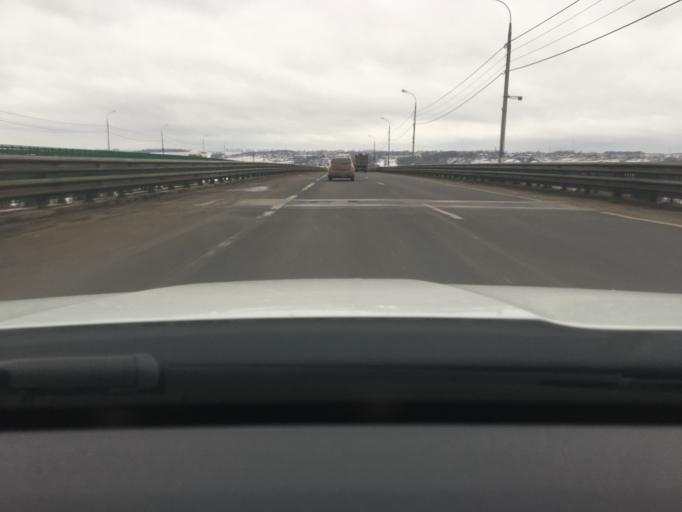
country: RU
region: Moskovskaya
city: Danki
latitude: 54.8702
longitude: 37.5038
